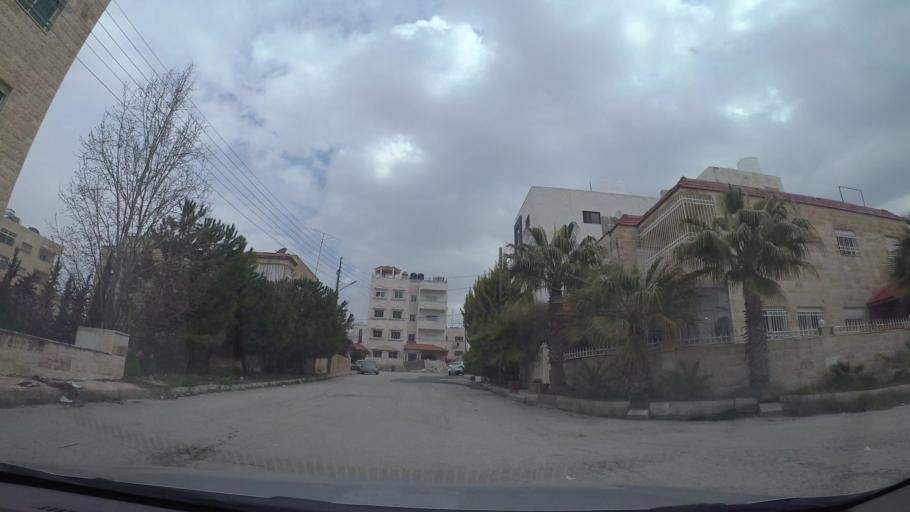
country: JO
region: Amman
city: Umm as Summaq
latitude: 31.8971
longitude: 35.8431
